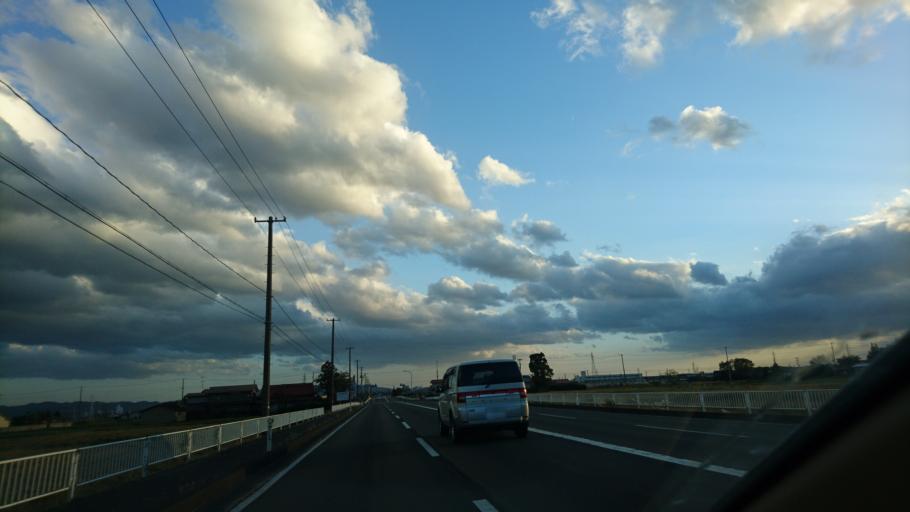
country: JP
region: Iwate
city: Mizusawa
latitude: 39.1619
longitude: 141.1329
